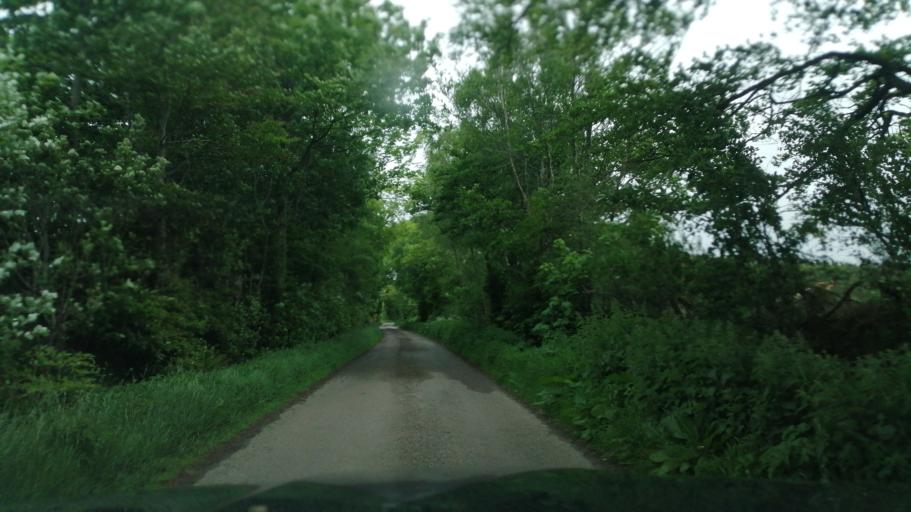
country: GB
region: Scotland
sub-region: Moray
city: Keith
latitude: 57.5637
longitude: -2.8618
